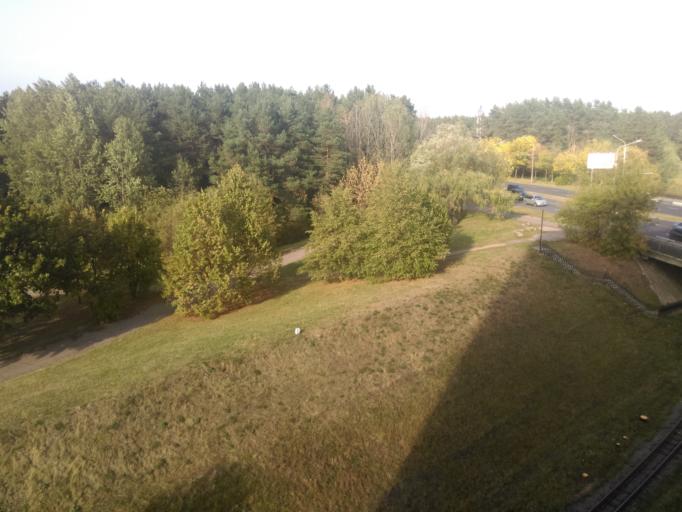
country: BY
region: Minsk
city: Minsk
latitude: 53.9119
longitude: 27.6336
